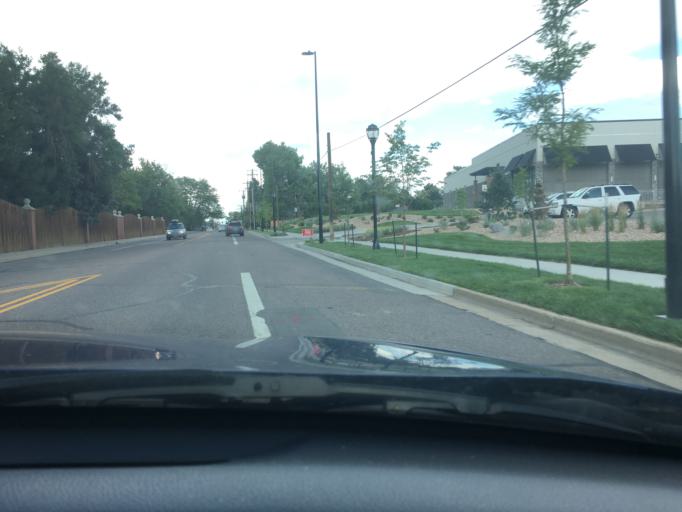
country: US
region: Colorado
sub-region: Jefferson County
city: Applewood
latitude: 39.7671
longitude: -105.1412
